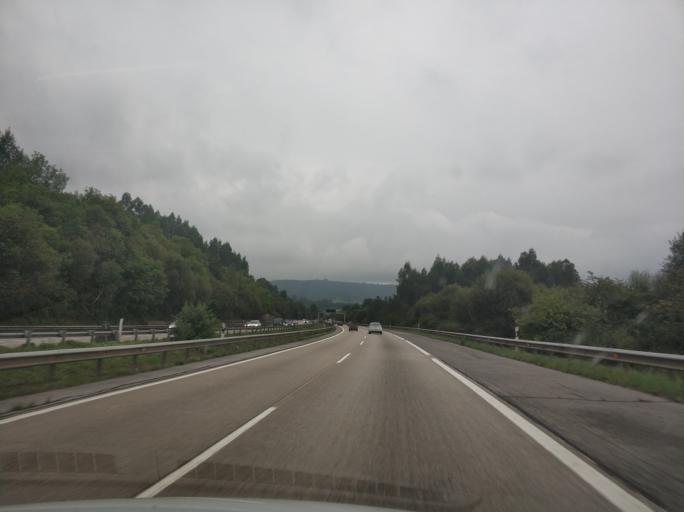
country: ES
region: Asturias
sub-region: Province of Asturias
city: Lugones
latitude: 43.4826
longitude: -5.7887
